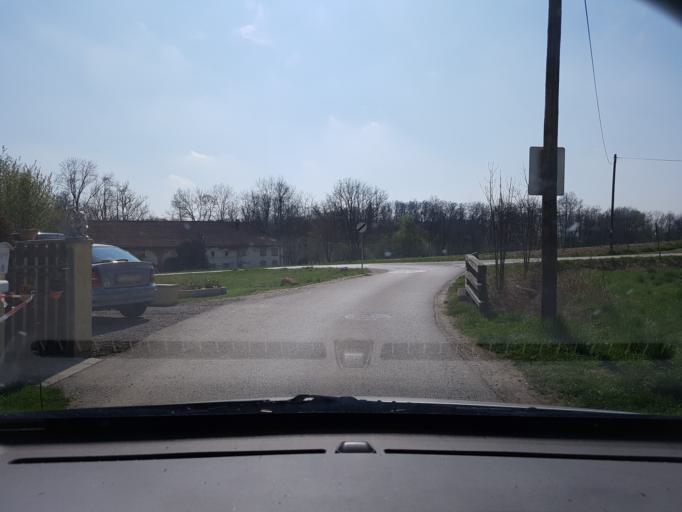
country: AT
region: Upper Austria
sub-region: Politischer Bezirk Linz-Land
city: Ansfelden
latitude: 48.1870
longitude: 14.3304
